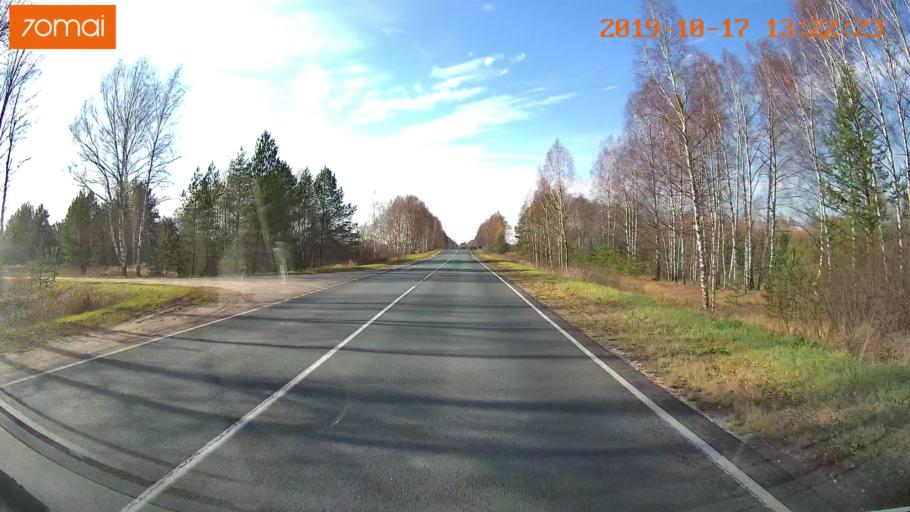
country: RU
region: Rjazan
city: Gus'-Zheleznyy
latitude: 55.0858
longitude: 41.0044
